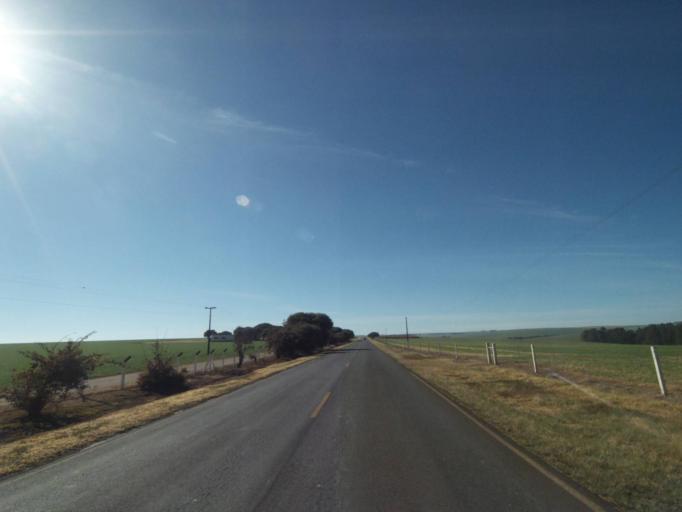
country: BR
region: Parana
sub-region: Tibagi
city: Tibagi
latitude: -24.5249
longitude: -50.3736
